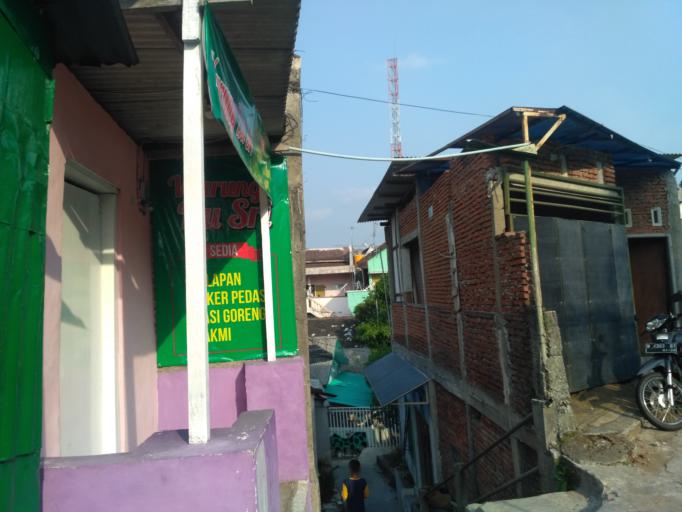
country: ID
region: East Java
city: Malang
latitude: -7.9598
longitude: 112.6258
